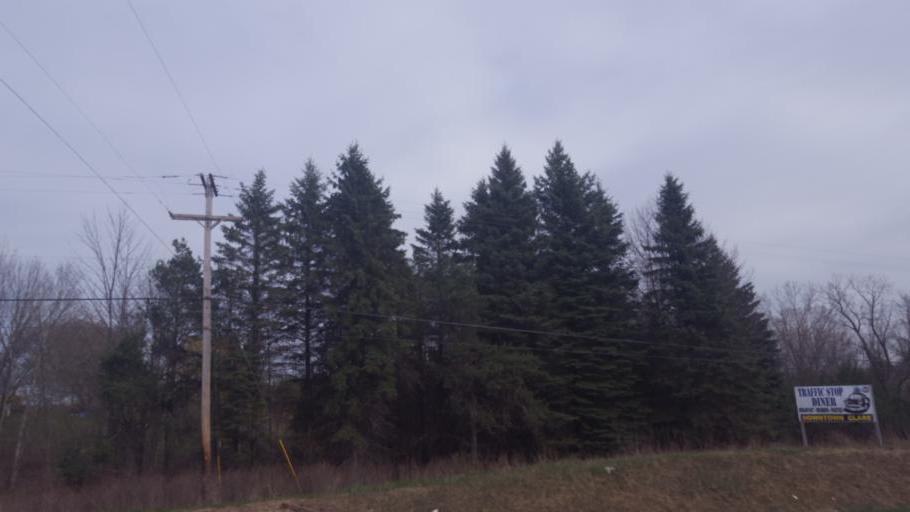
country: US
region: Michigan
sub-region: Clare County
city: Clare
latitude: 43.8575
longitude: -84.7681
